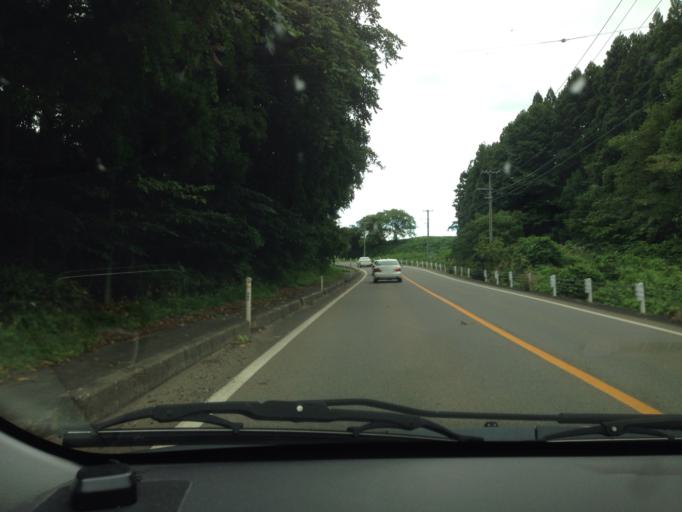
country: JP
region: Fukushima
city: Kitakata
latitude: 37.5772
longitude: 139.9353
